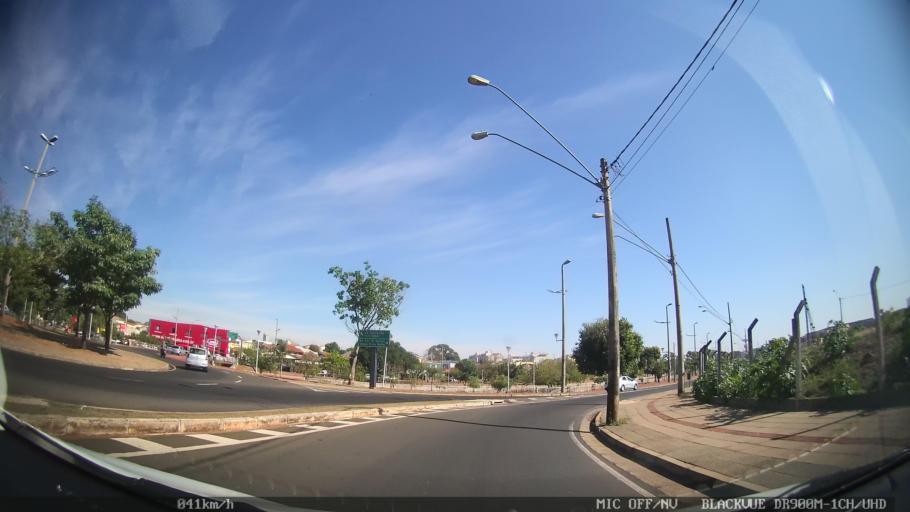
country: BR
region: Sao Paulo
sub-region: Sao Jose Do Rio Preto
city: Sao Jose do Rio Preto
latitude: -20.7857
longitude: -49.3763
